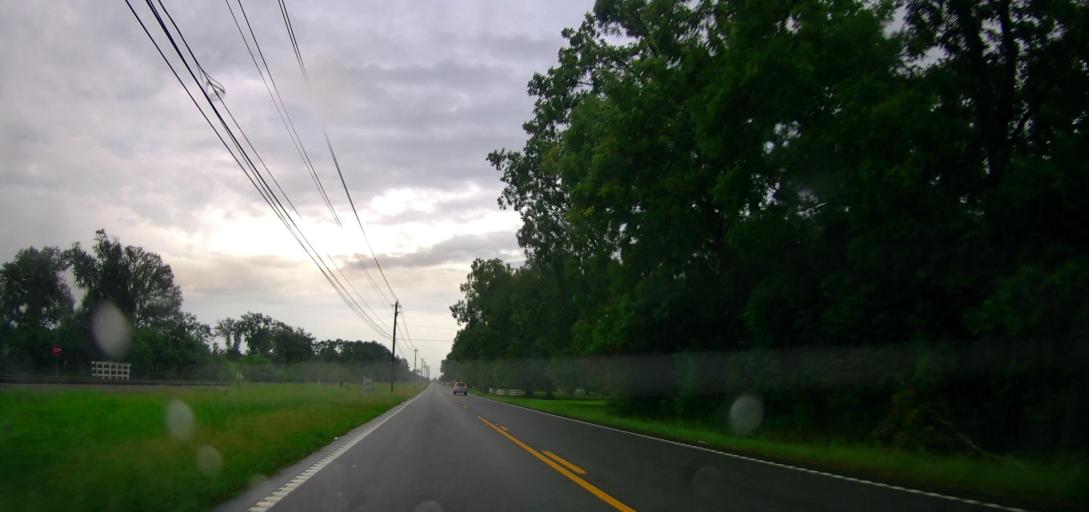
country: US
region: Georgia
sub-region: Ware County
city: Deenwood
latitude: 31.2452
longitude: -82.3737
